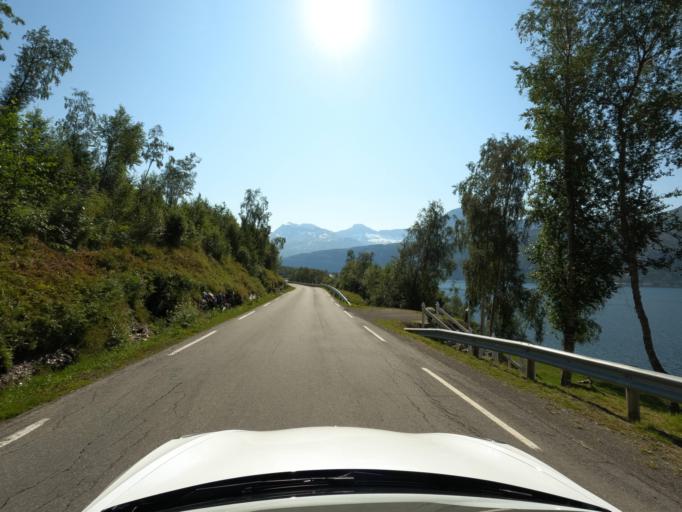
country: NO
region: Nordland
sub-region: Narvik
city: Narvik
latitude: 68.3424
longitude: 17.2777
